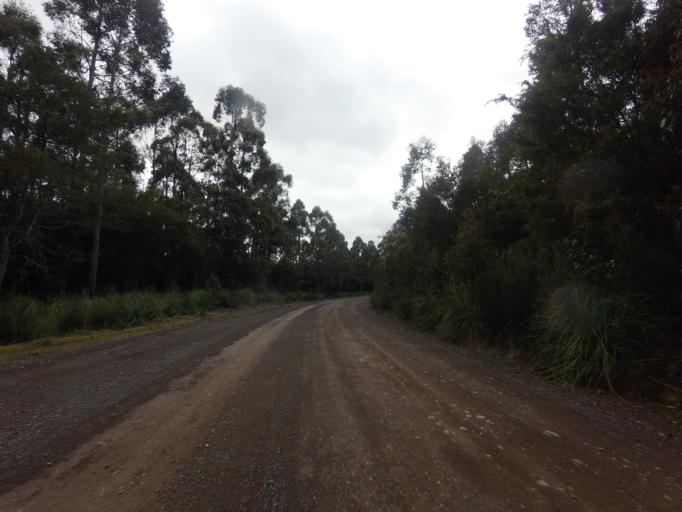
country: AU
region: Tasmania
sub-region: Huon Valley
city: Geeveston
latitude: -43.4681
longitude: 146.8942
